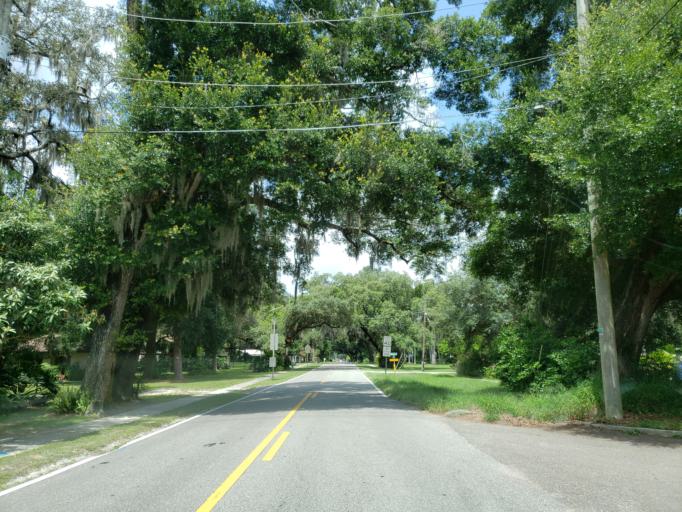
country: US
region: Florida
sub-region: Hillsborough County
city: Seffner
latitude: 27.9962
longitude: -82.2817
